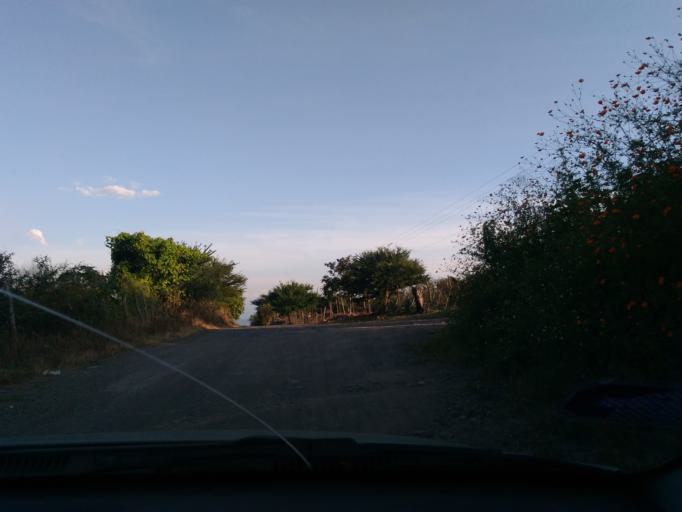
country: MX
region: Jalisco
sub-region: Tonila
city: San Marcos
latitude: 19.4572
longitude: -103.5195
